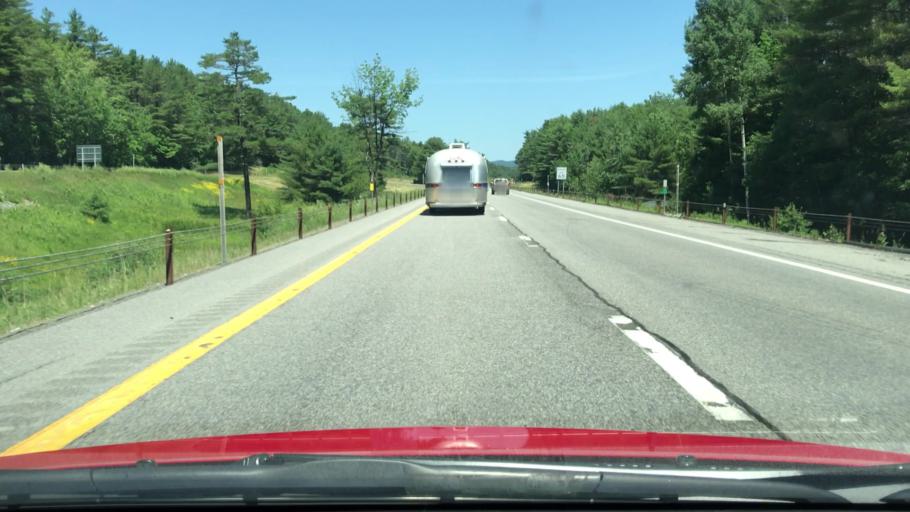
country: US
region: New York
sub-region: Essex County
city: Elizabethtown
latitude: 44.2943
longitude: -73.5317
